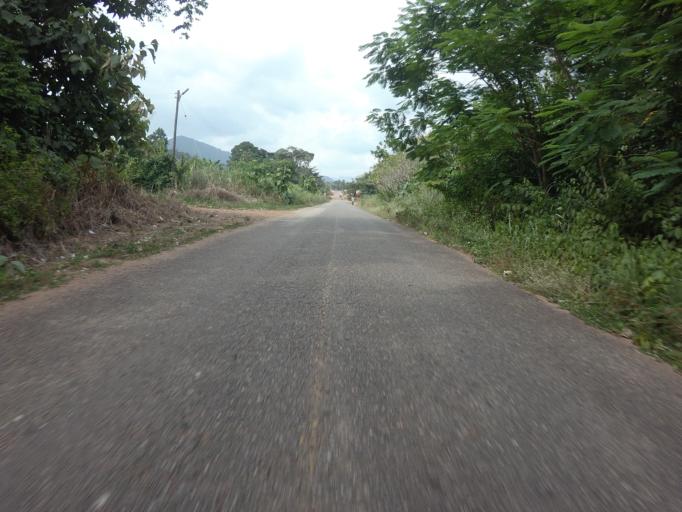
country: GH
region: Volta
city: Ho
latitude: 6.6686
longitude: 0.3525
